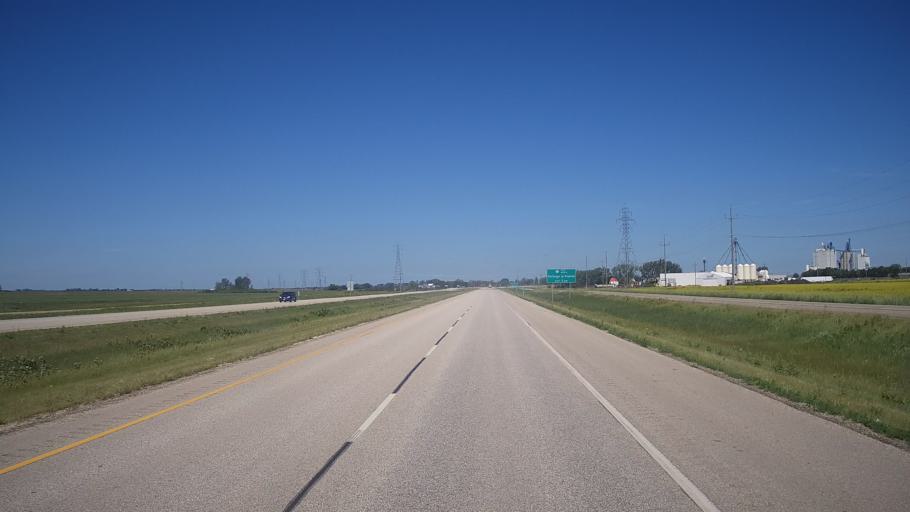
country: CA
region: Manitoba
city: Portage la Prairie
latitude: 49.9587
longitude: -98.3402
